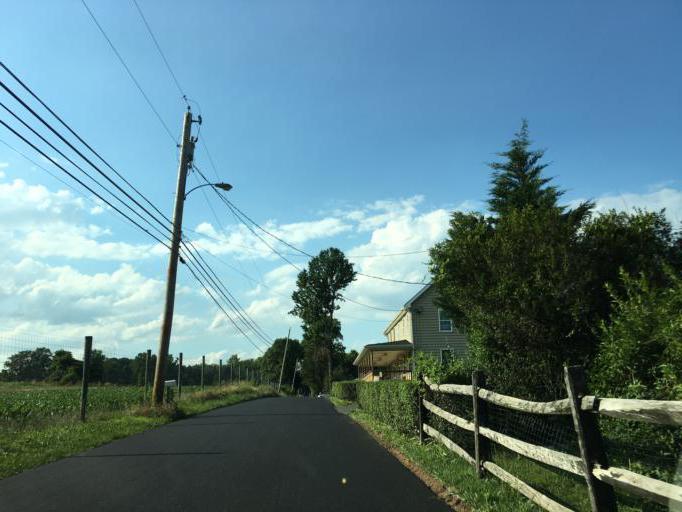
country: US
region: Maryland
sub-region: Baltimore County
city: Kingsville
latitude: 39.4541
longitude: -76.4385
